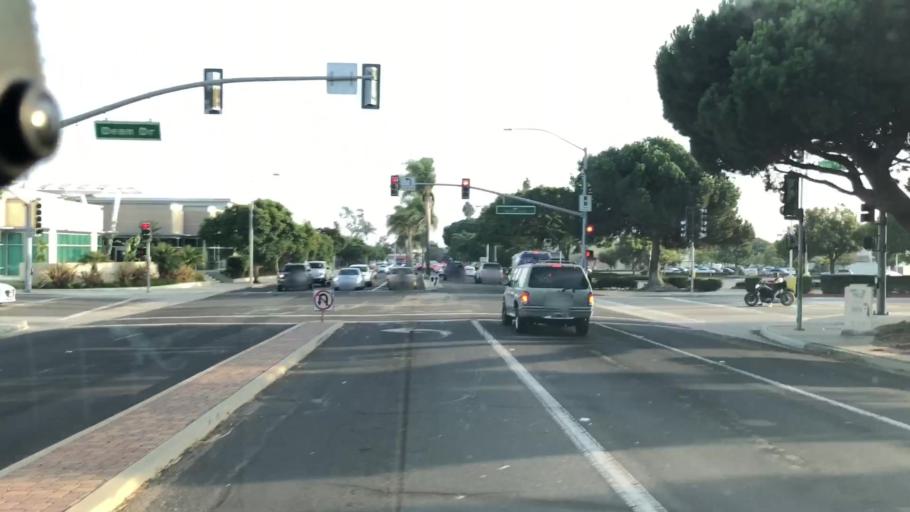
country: US
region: California
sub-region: Ventura County
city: Ventura
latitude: 34.2676
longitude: -119.2466
